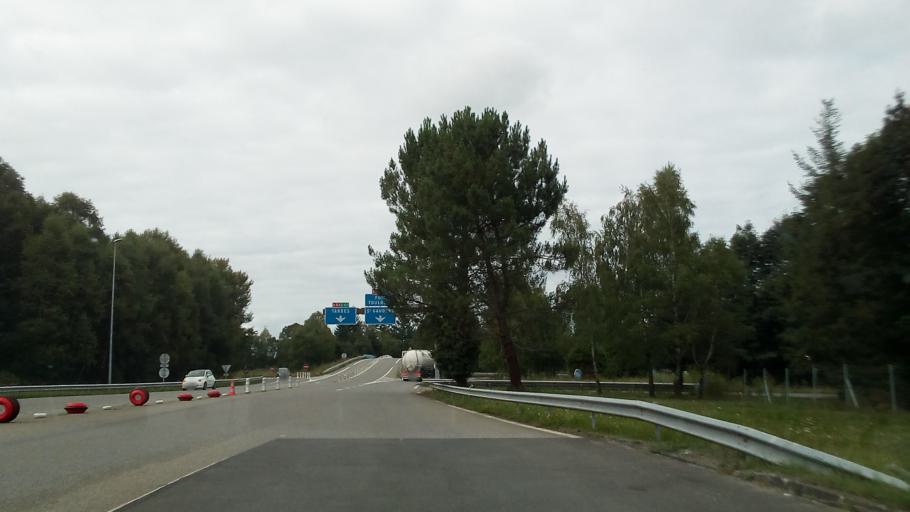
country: FR
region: Midi-Pyrenees
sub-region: Departement des Hautes-Pyrenees
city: La Barthe-de-Neste
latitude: 43.0979
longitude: 0.3904
